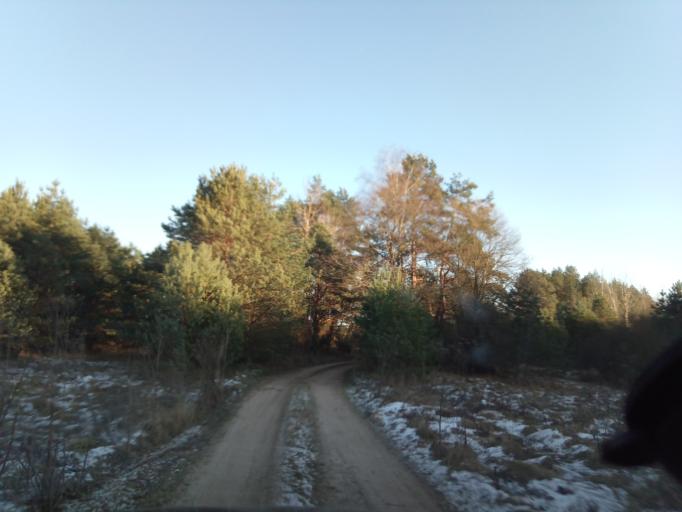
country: LT
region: Alytaus apskritis
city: Druskininkai
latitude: 53.9724
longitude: 23.9605
